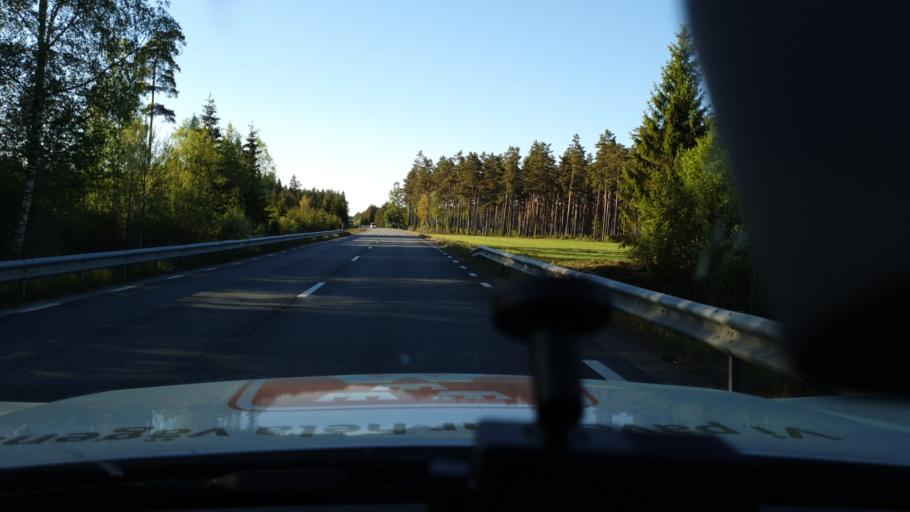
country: SE
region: Joenkoeping
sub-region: Eksjo Kommun
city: Eksjoe
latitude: 57.6156
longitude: 14.9703
